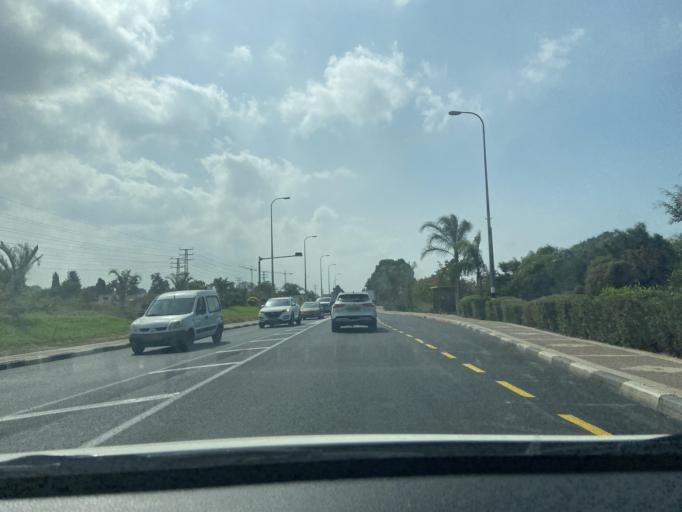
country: IL
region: Northern District
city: Nahariya
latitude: 33.0256
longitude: 35.1037
